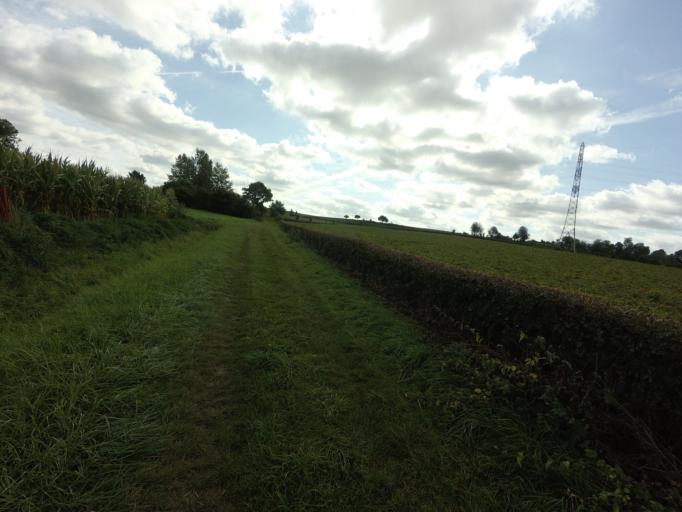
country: NL
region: Limburg
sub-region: Gemeente Voerendaal
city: Klimmen
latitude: 50.8570
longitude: 5.8996
